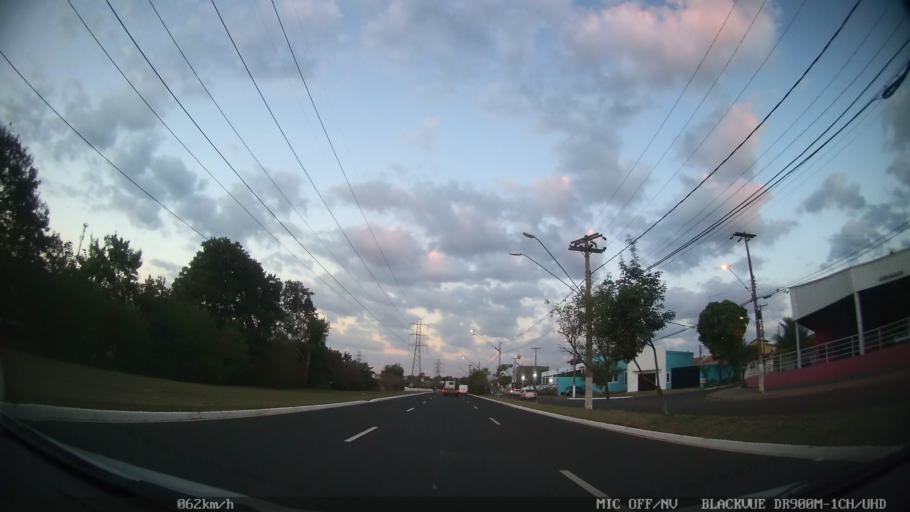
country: BR
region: Sao Paulo
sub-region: Ribeirao Preto
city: Ribeirao Preto
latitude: -21.2110
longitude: -47.7795
